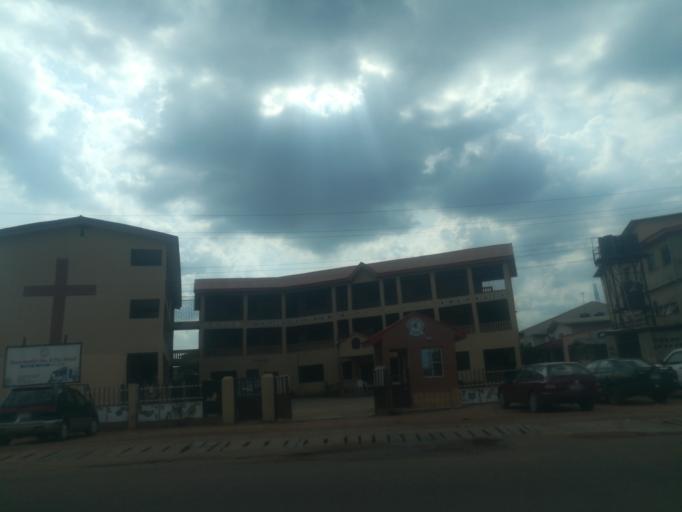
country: NG
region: Ogun
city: Abeokuta
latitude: 7.1412
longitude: 3.3397
